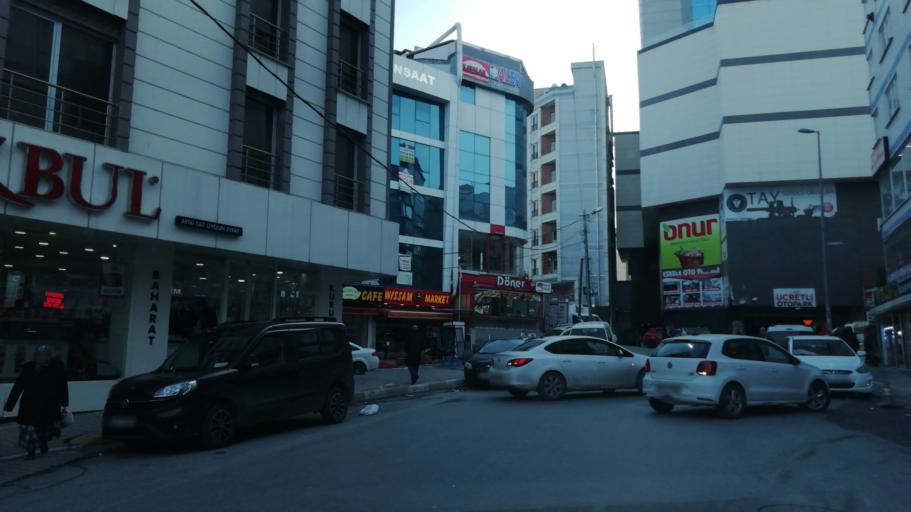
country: TR
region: Istanbul
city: Esenyurt
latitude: 41.0350
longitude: 28.6814
